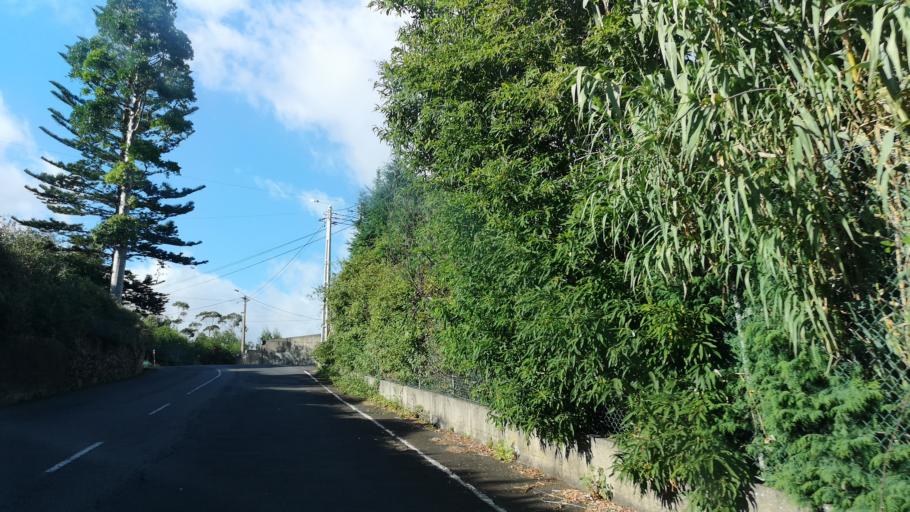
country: PT
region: Madeira
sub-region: Santa Cruz
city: Camacha
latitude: 32.6613
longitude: -16.8360
